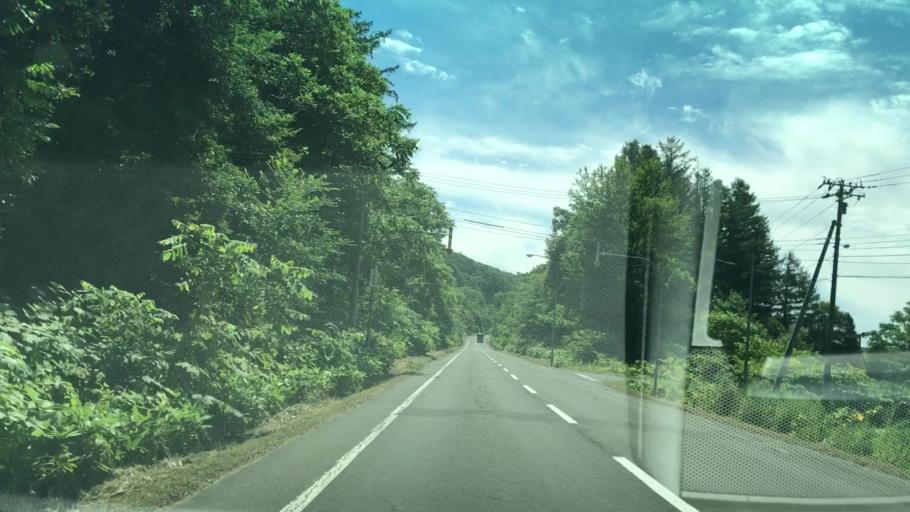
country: JP
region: Hokkaido
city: Shimo-furano
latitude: 42.9706
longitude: 142.4230
